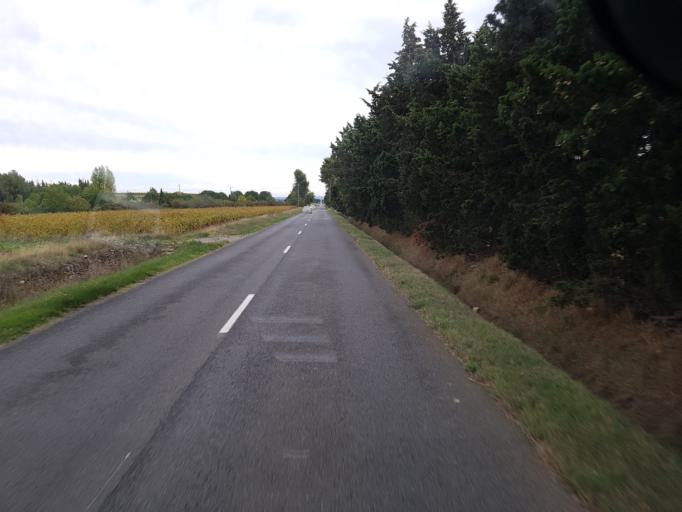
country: FR
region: Languedoc-Roussillon
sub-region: Departement de l'Aude
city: Caunes-Minervois
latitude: 43.3080
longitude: 2.5163
